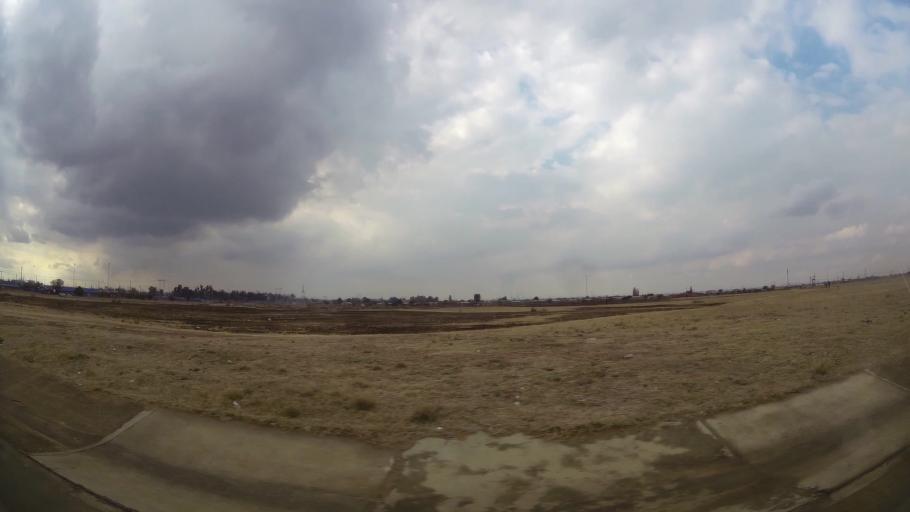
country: ZA
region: Orange Free State
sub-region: Fezile Dabi District Municipality
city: Sasolburg
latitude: -26.8577
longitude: 27.8674
